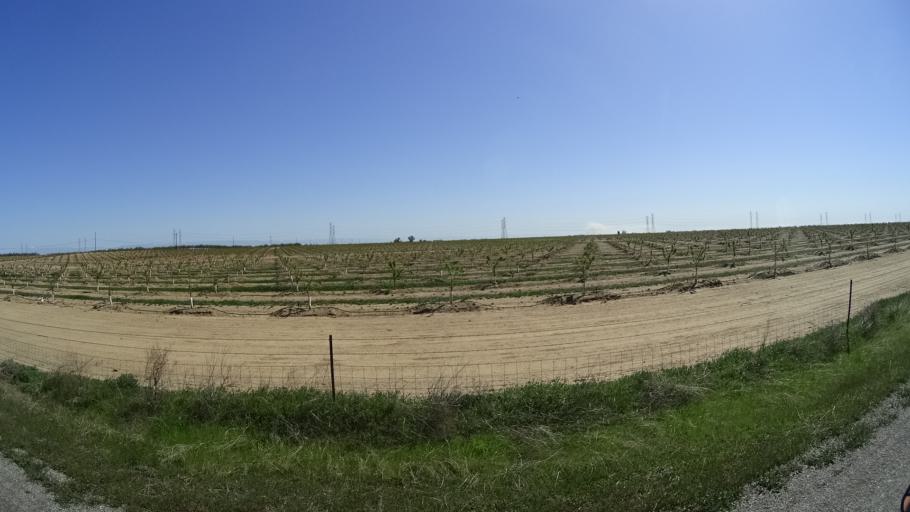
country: US
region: California
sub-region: Glenn County
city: Orland
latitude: 39.6671
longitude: -122.2717
